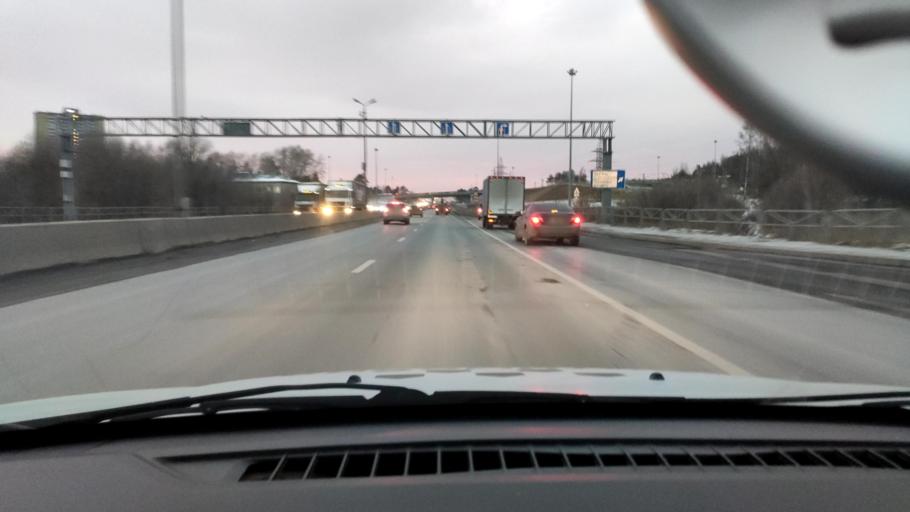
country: RU
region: Perm
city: Kondratovo
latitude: 58.0373
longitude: 56.0496
